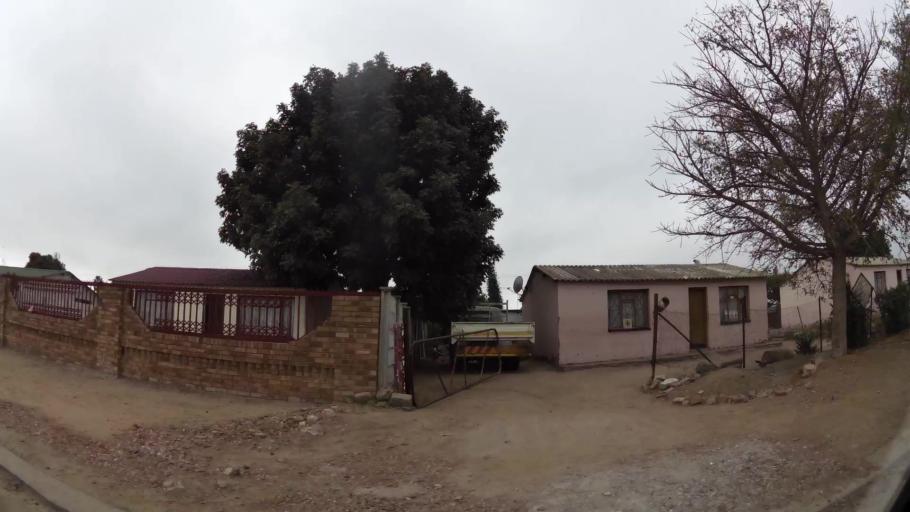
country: ZA
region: Limpopo
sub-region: Capricorn District Municipality
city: Polokwane
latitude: -23.8387
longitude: 29.3916
